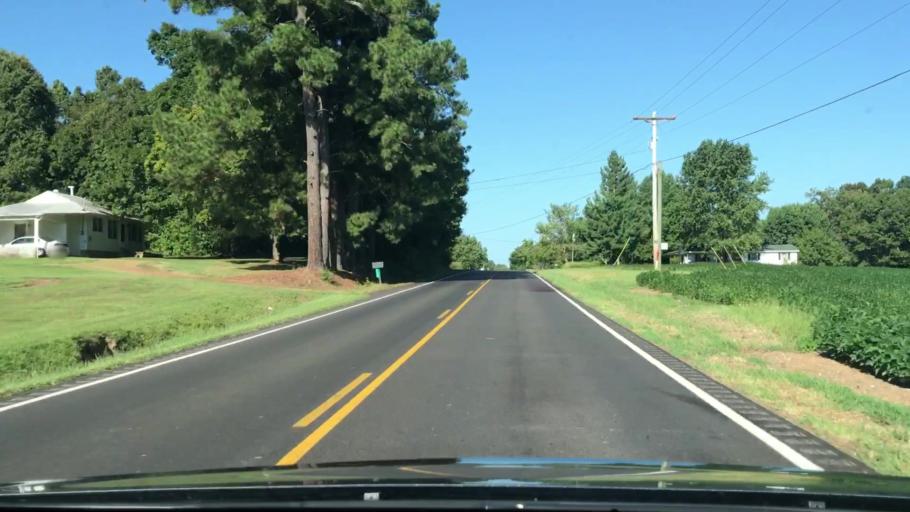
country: US
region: Kentucky
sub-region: Marshall County
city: Benton
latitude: 36.7647
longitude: -88.3326
